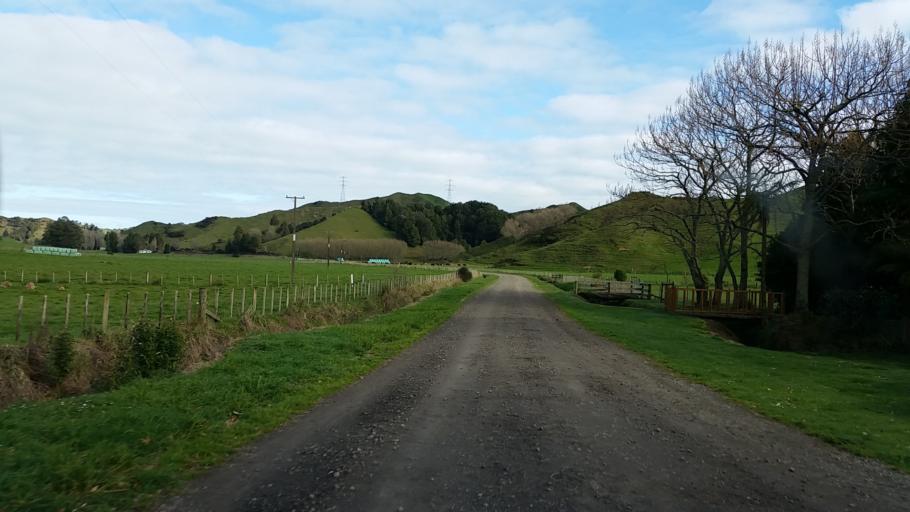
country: NZ
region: Taranaki
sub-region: South Taranaki District
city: Eltham
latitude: -39.2501
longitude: 174.5412
